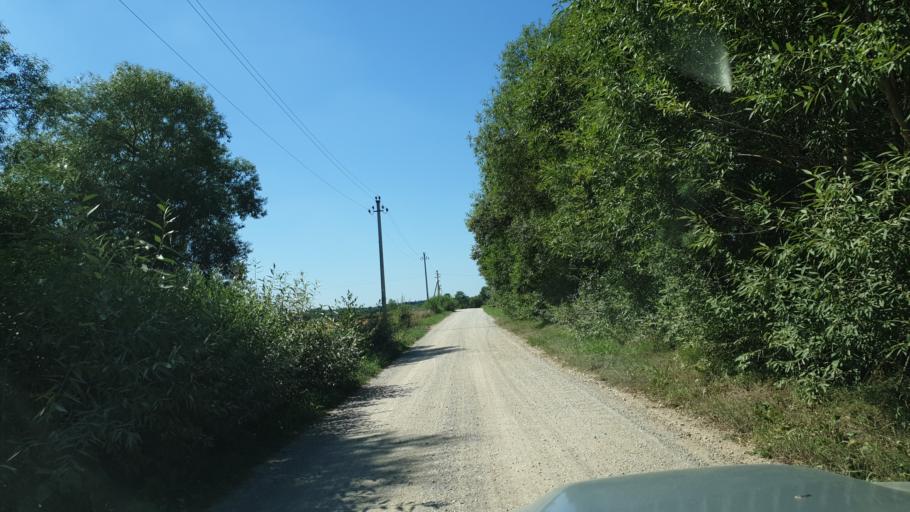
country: LT
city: Sirvintos
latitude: 54.9166
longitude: 24.9139
